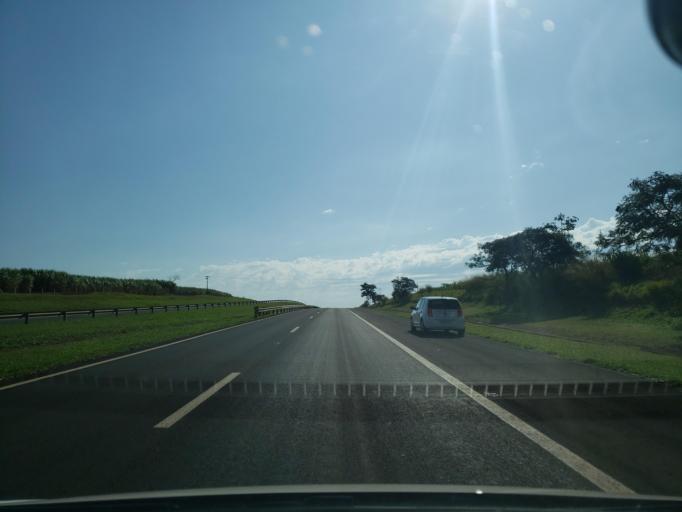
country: BR
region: Sao Paulo
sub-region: Promissao
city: Promissao
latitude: -21.5336
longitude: -49.9808
